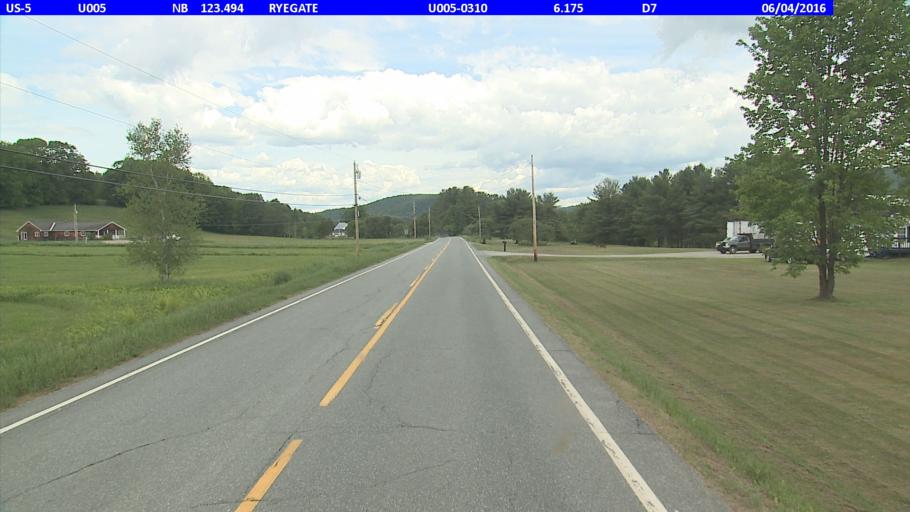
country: US
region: New Hampshire
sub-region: Grafton County
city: Woodsville
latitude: 44.2403
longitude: -72.0546
